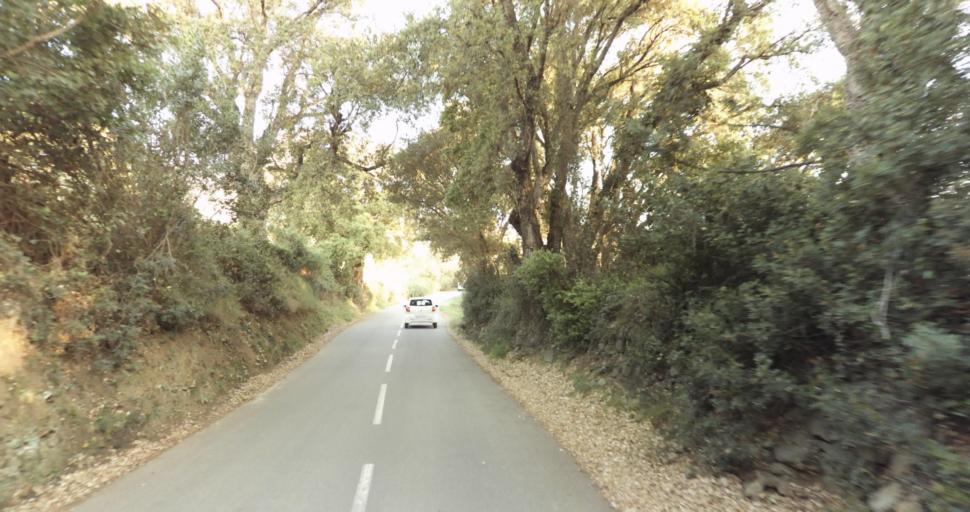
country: FR
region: Corsica
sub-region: Departement de la Haute-Corse
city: Biguglia
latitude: 42.6240
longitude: 9.4432
